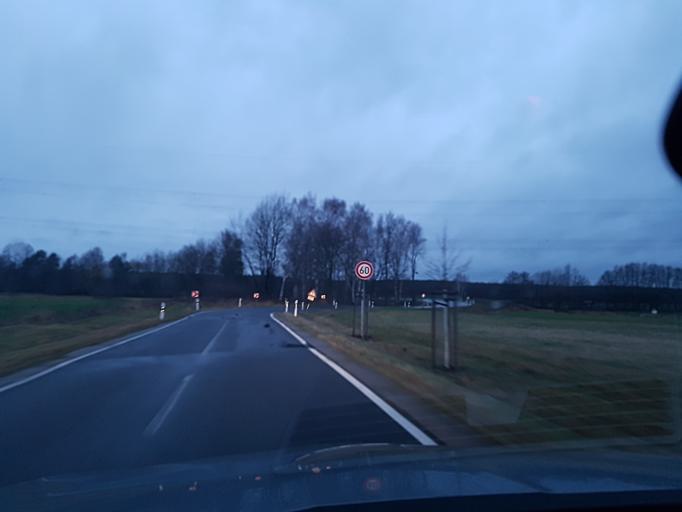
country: DE
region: Brandenburg
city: Bad Liebenwerda
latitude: 51.5438
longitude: 13.4451
